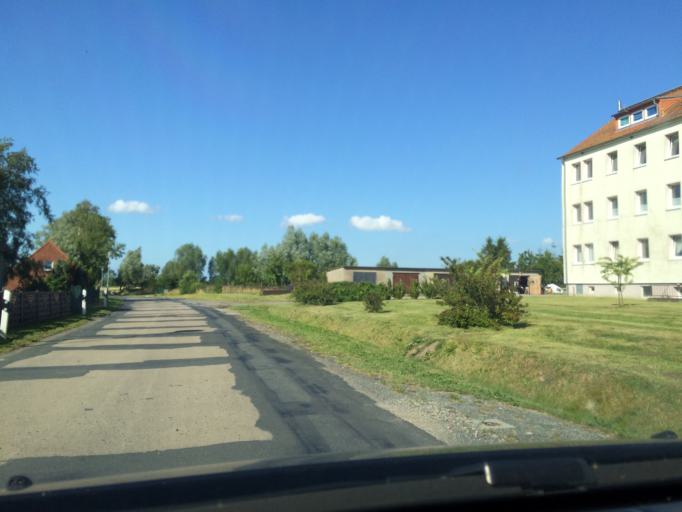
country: DE
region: Mecklenburg-Vorpommern
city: Niepars
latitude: 54.3475
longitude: 12.8972
